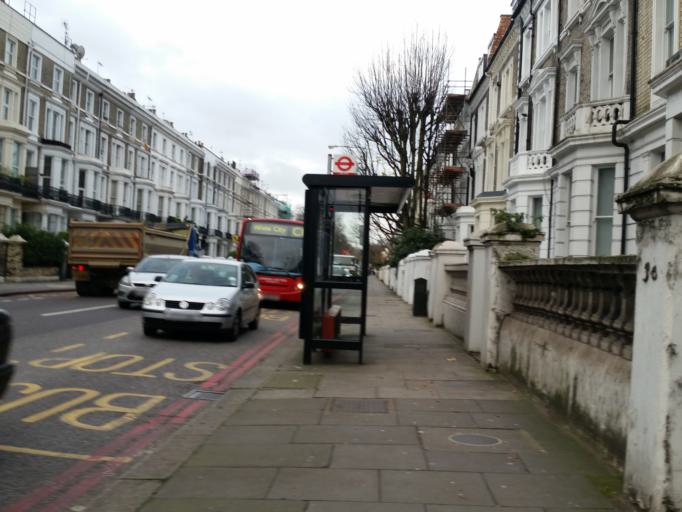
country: GB
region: England
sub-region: Greater London
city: Hammersmith
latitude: 51.5019
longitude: -0.2135
